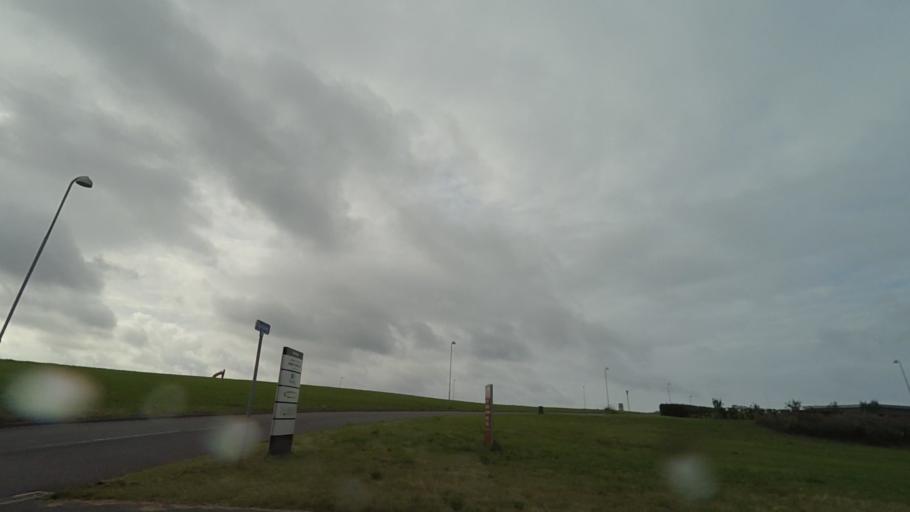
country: DK
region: Central Jutland
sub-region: Syddjurs Kommune
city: Ronde
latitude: 56.3104
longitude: 10.4557
